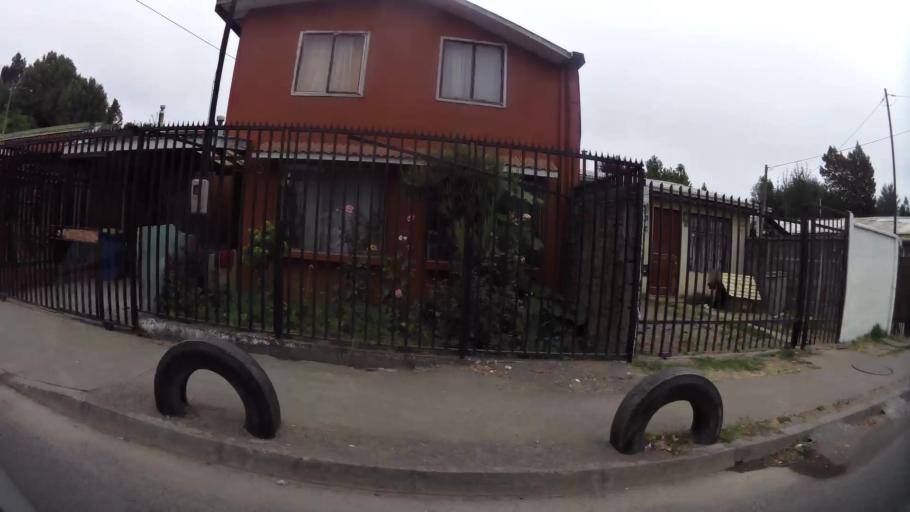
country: CL
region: Biobio
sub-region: Provincia de Concepcion
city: Concepcion
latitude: -36.8370
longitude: -73.0025
